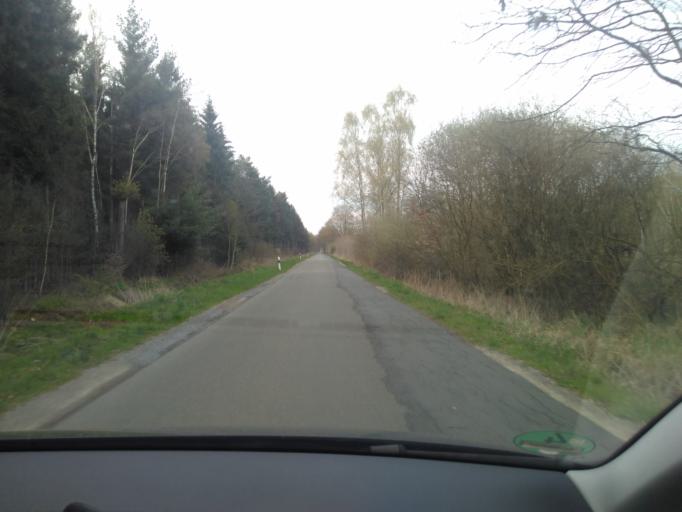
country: DE
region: Lower Saxony
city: Adelheidsdorf
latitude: 52.5309
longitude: 10.0317
